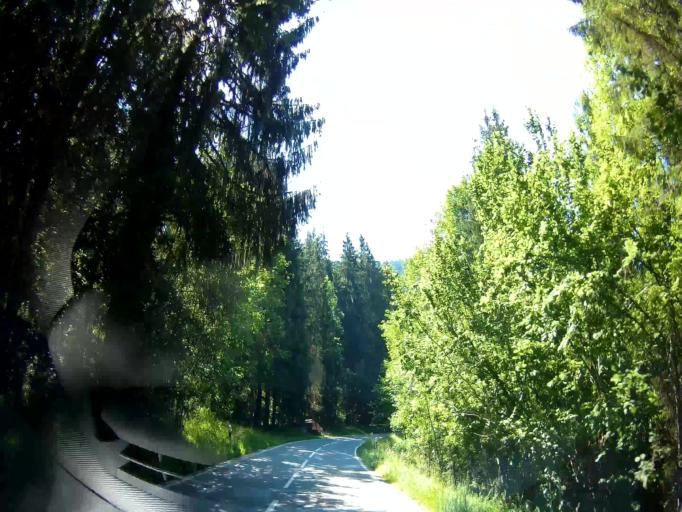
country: DE
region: Bavaria
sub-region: Upper Bavaria
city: Marktschellenberg
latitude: 47.6441
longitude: 13.0593
